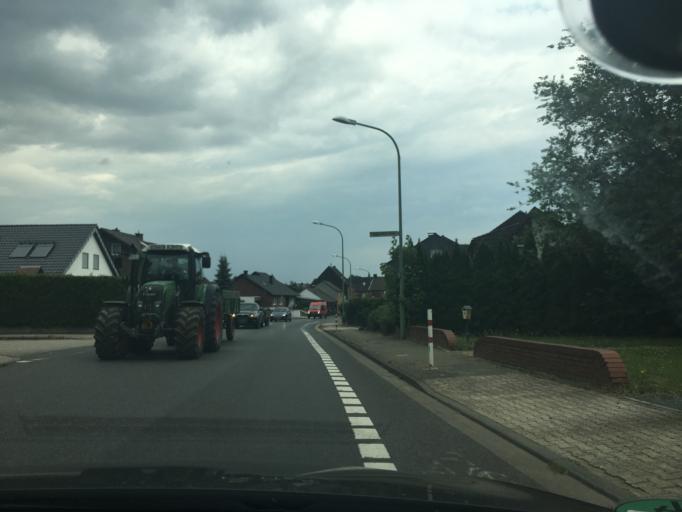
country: DE
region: North Rhine-Westphalia
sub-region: Regierungsbezirk Koln
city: Dueren
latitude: 50.8359
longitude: 6.4834
